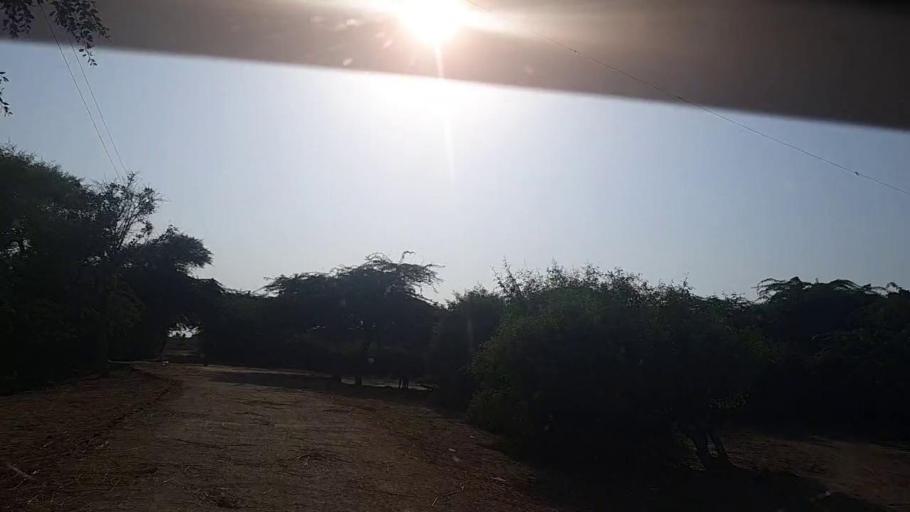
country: PK
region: Sindh
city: Talhar
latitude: 24.8553
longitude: 68.8522
